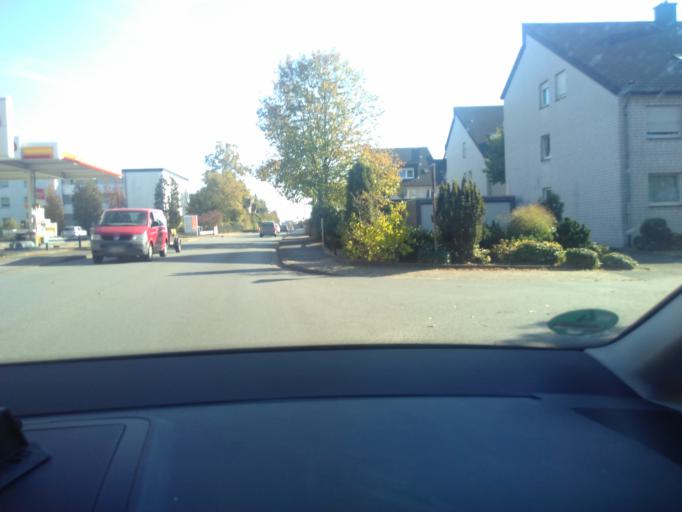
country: DE
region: North Rhine-Westphalia
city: Halle
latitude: 52.0578
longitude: 8.3676
